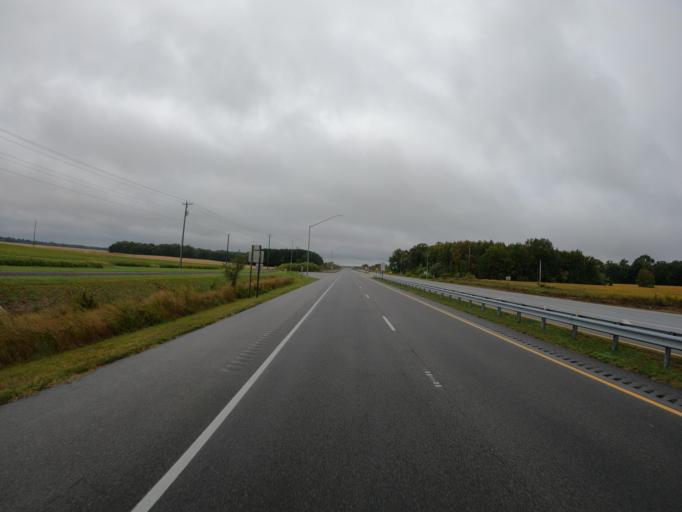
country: US
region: Maryland
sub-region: Queen Anne's County
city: Centreville
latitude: 38.9311
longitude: -76.0202
